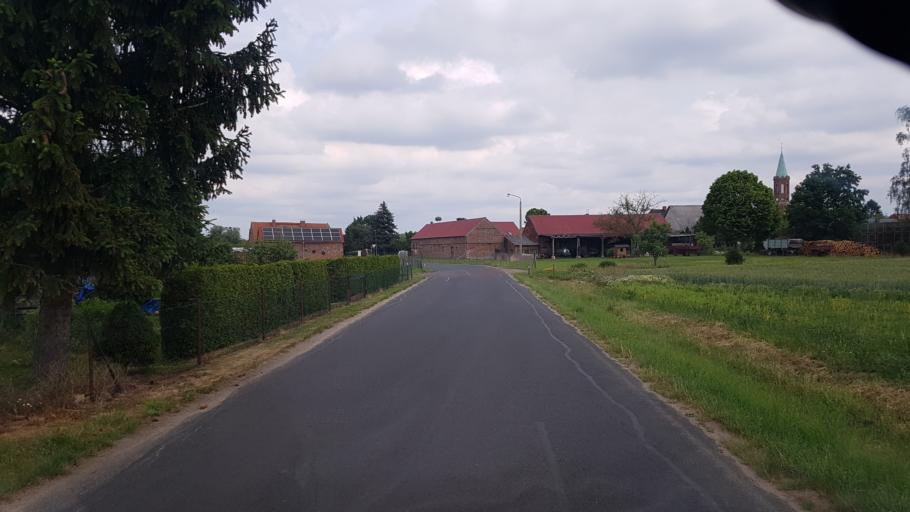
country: DE
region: Brandenburg
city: Lebusa
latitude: 51.8233
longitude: 13.4544
